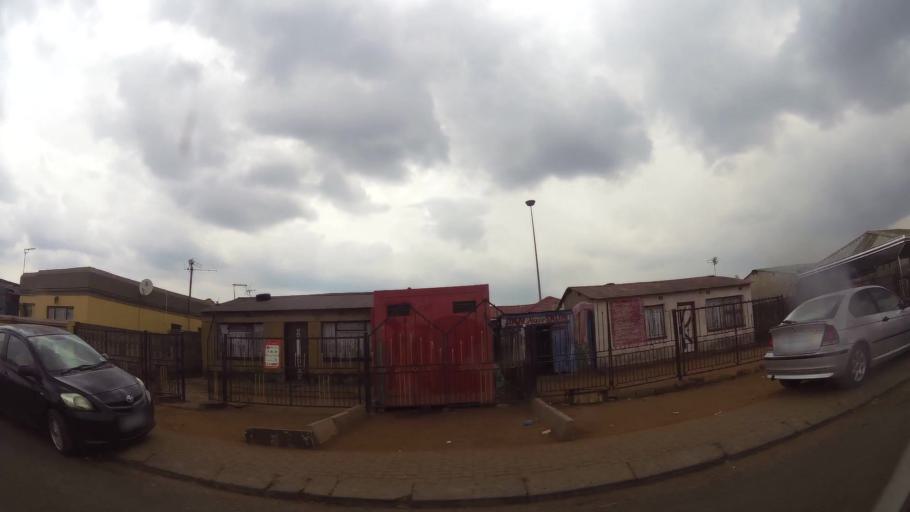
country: ZA
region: Gauteng
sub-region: Ekurhuleni Metropolitan Municipality
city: Germiston
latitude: -26.3533
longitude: 28.1498
